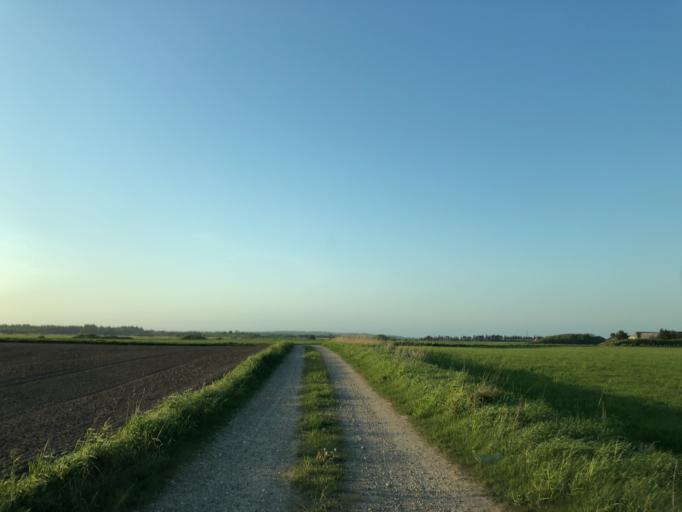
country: DK
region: Central Jutland
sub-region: Holstebro Kommune
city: Ulfborg
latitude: 56.2502
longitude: 8.1533
